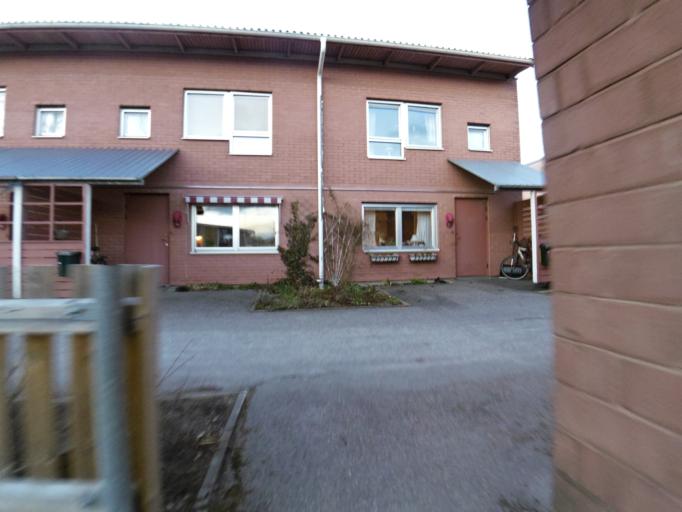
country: SE
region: Gaevleborg
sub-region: Gavle Kommun
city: Gavle
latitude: 60.6605
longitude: 17.1643
